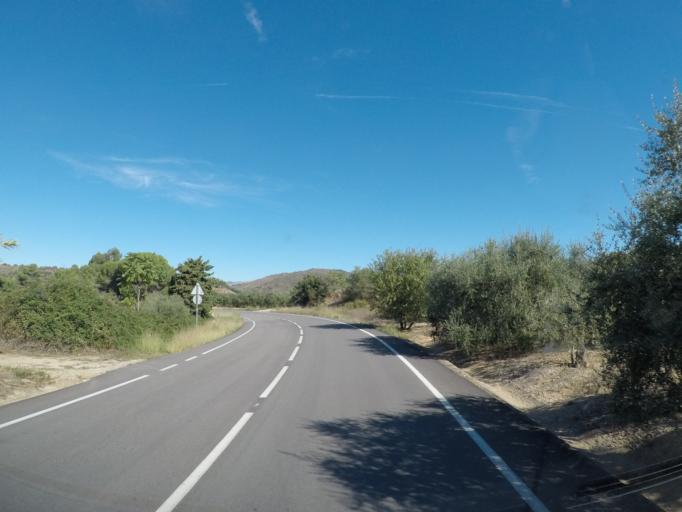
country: ES
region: Catalonia
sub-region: Provincia de Tarragona
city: Falset
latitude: 41.1528
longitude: 0.8180
